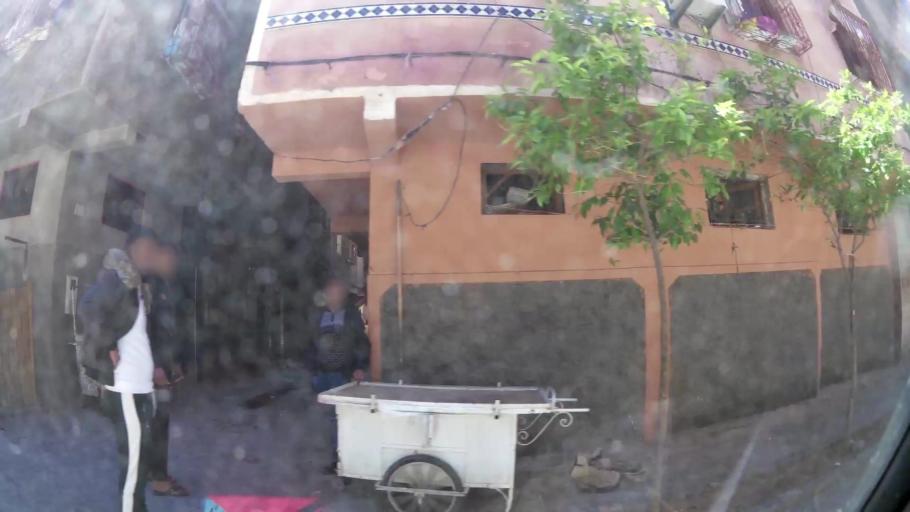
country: MA
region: Marrakech-Tensift-Al Haouz
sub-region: Marrakech
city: Marrakesh
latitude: 31.6567
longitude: -7.9910
